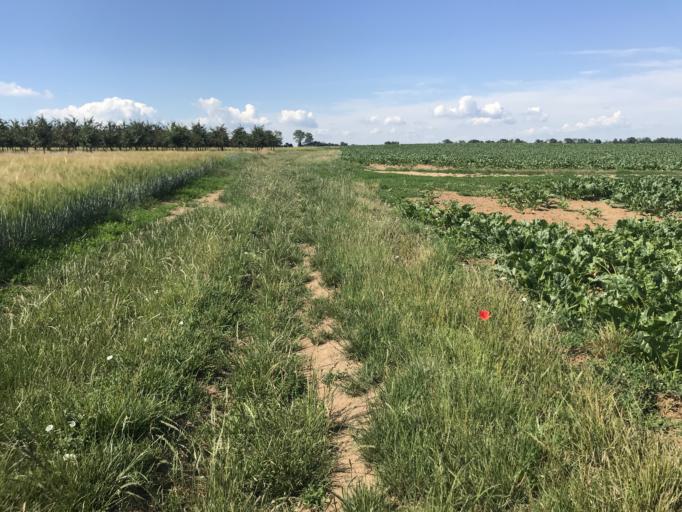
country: DE
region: Rheinland-Pfalz
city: Stadecken-Elsheim
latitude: 49.9355
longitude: 8.1253
